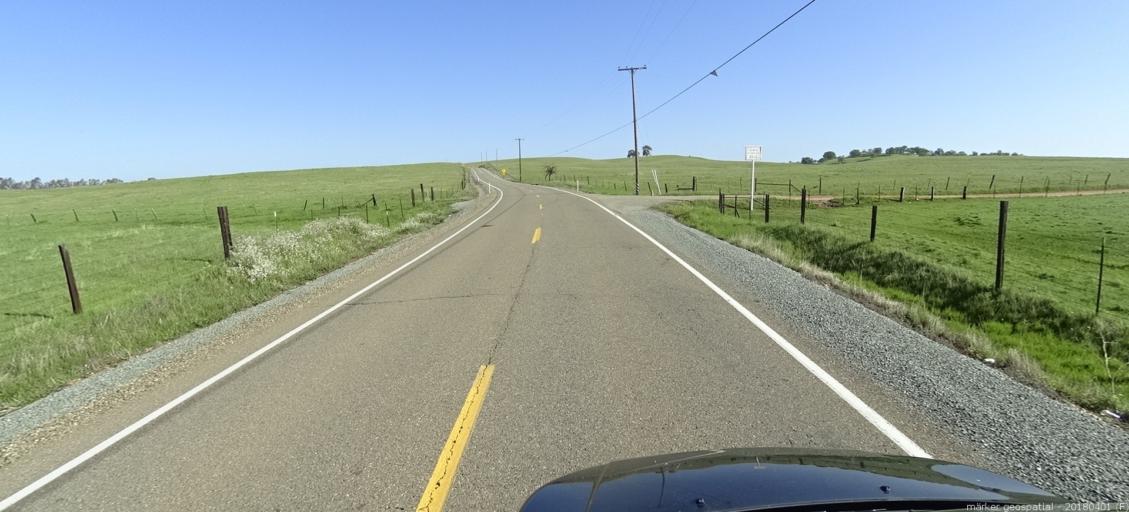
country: US
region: California
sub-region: Sacramento County
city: Rancho Murieta
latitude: 38.4377
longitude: -121.0487
